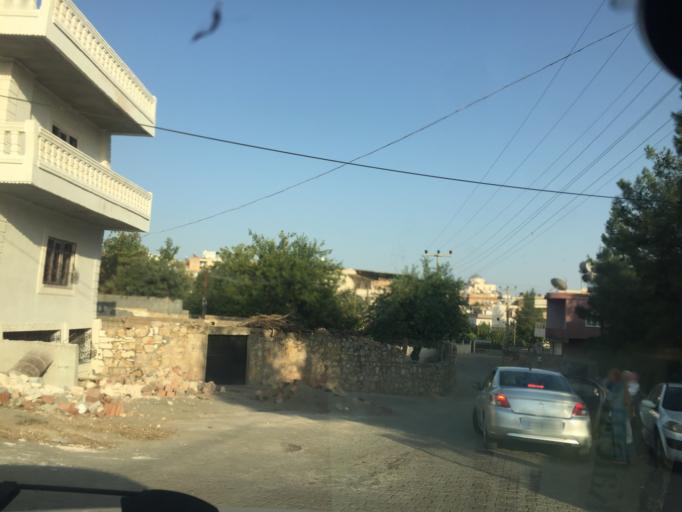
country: TR
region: Mardin
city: Kindirip
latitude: 37.4483
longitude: 41.2175
